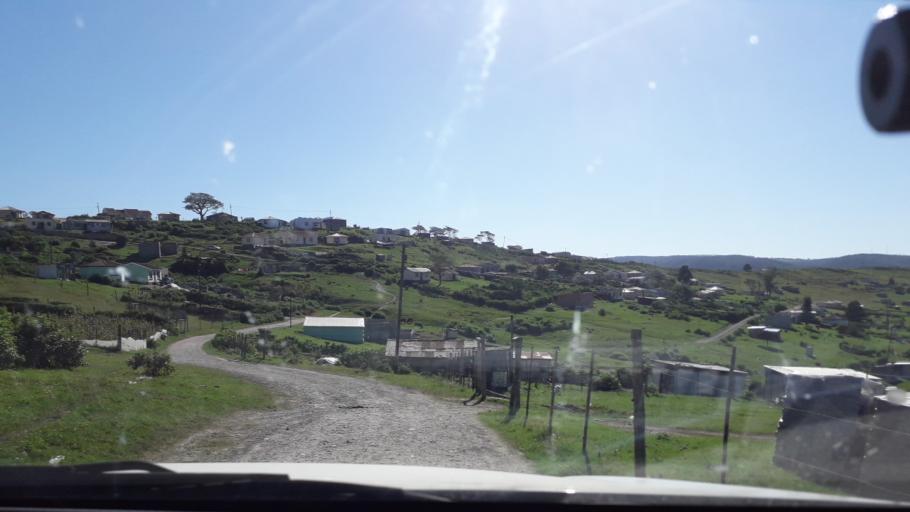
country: ZA
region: Eastern Cape
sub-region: Buffalo City Metropolitan Municipality
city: East London
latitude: -32.8455
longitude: 27.9904
